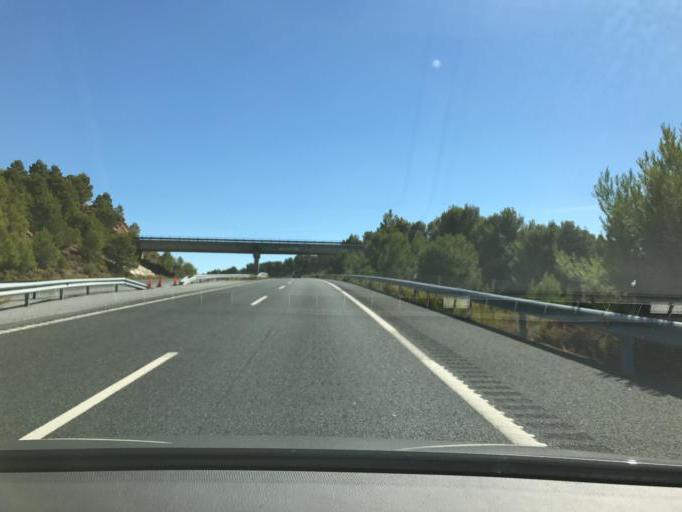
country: ES
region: Andalusia
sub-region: Provincia de Granada
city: Diezma
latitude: 37.3089
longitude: -3.3733
